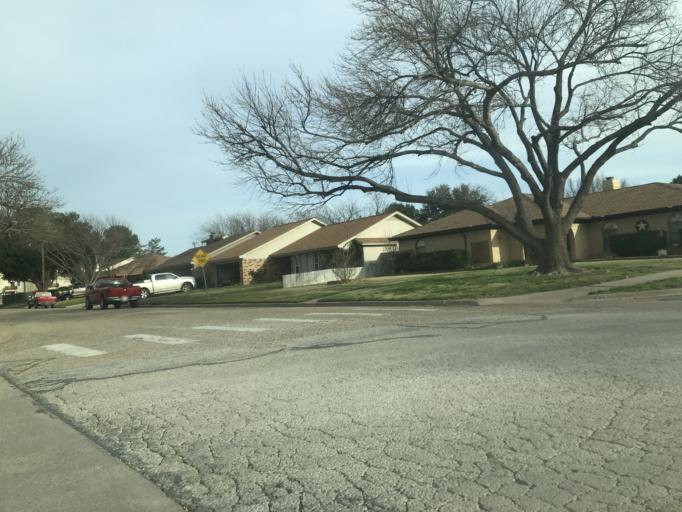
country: US
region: Texas
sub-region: Taylor County
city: Abilene
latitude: 32.3982
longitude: -99.7692
